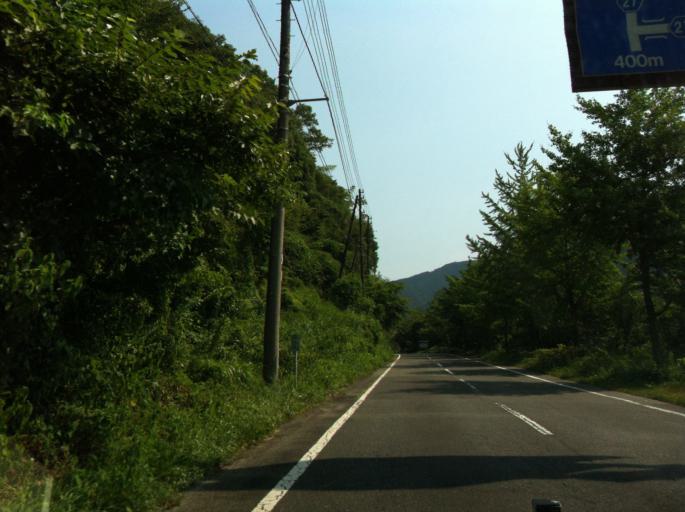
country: JP
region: Shizuoka
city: Shizuoka-shi
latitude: 35.1165
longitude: 138.3610
